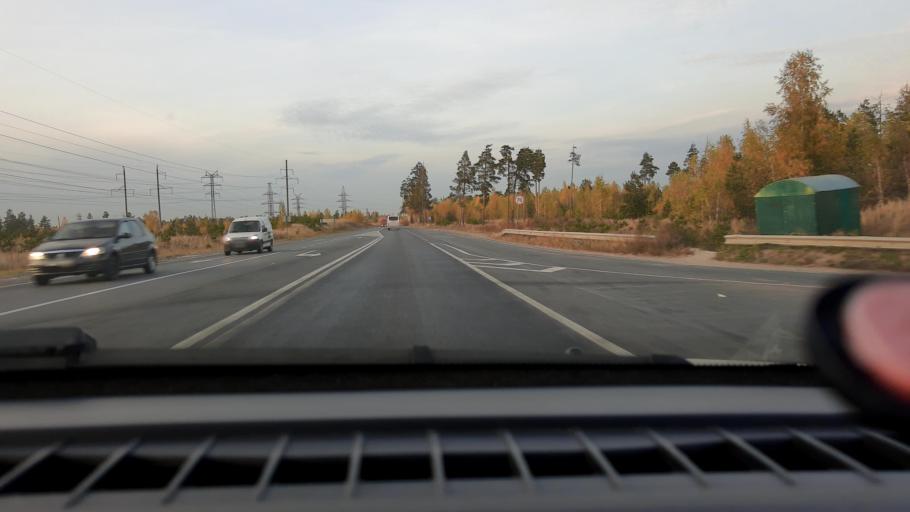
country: RU
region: Nizjnij Novgorod
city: Babino
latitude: 56.3225
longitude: 43.5591
